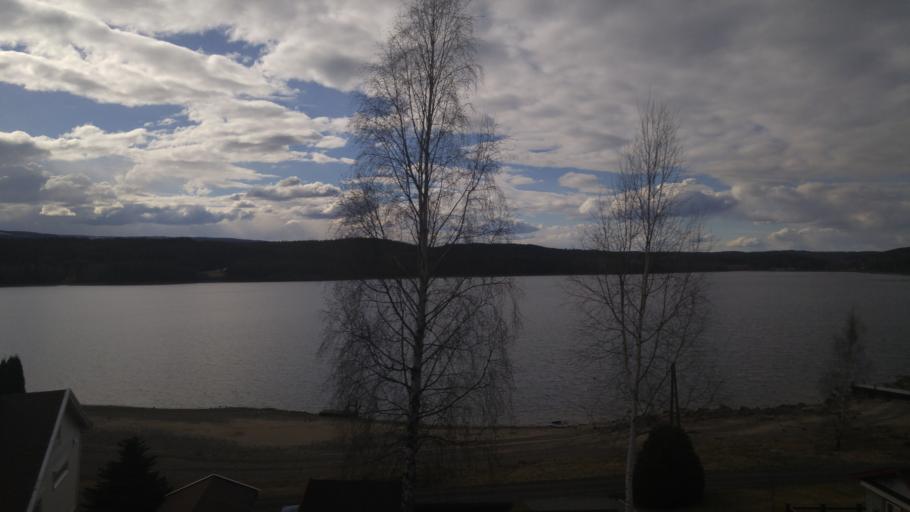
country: NO
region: Hedmark
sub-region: Stange
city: Stange
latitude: 60.5966
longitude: 11.2900
